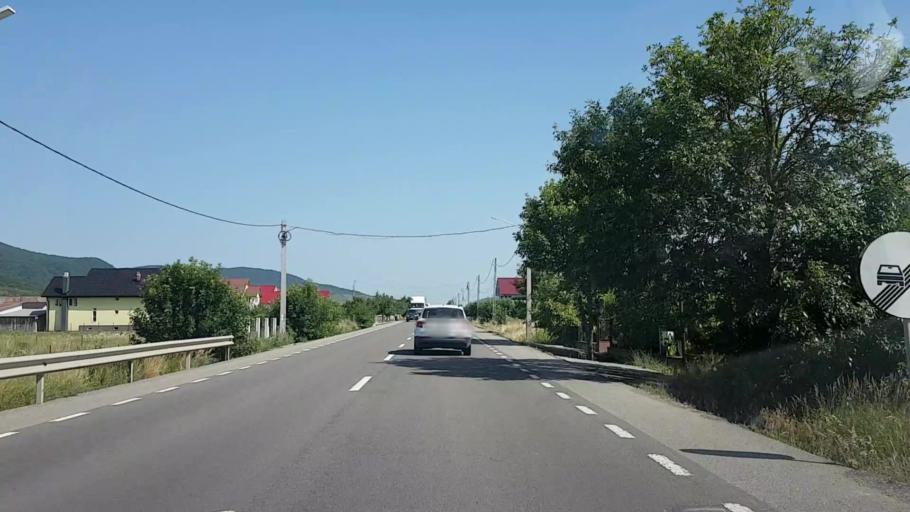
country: RO
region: Bistrita-Nasaud
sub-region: Comuna Sieu-Magherus
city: Sieu-Magherus
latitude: 47.1001
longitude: 24.3614
